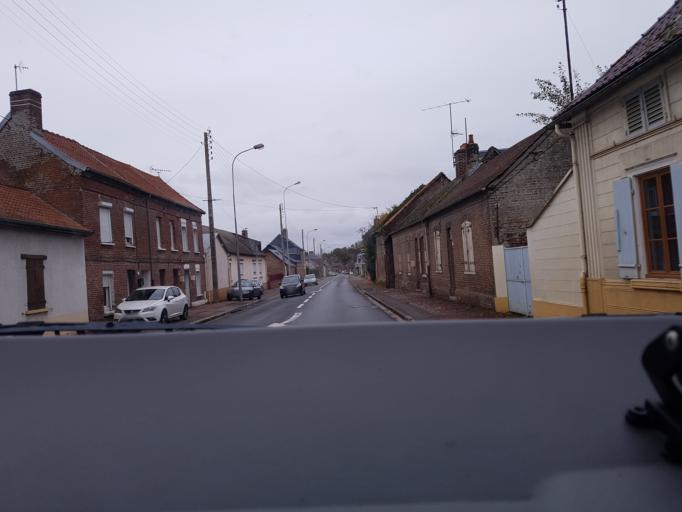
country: FR
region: Picardie
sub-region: Departement de la Somme
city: Abbeville
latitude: 50.1065
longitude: 1.7930
